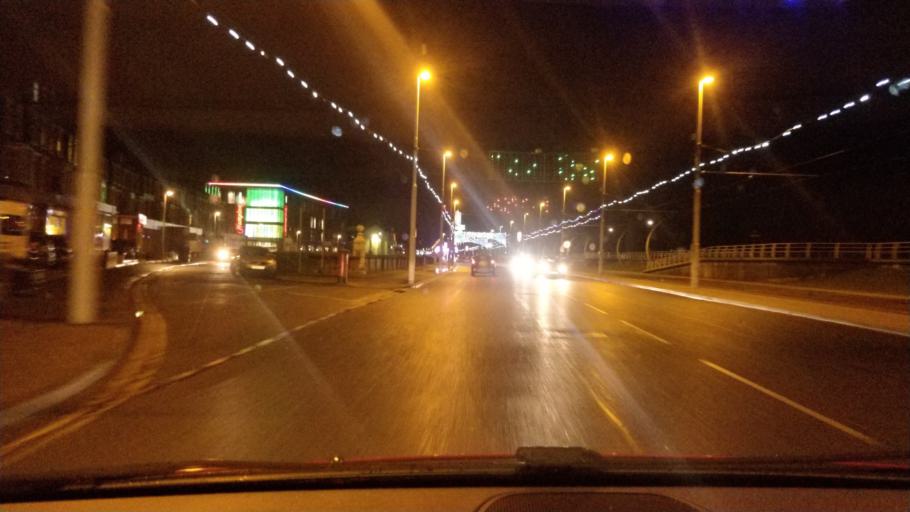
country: GB
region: England
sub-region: Blackpool
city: Blackpool
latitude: 53.7869
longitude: -3.0581
